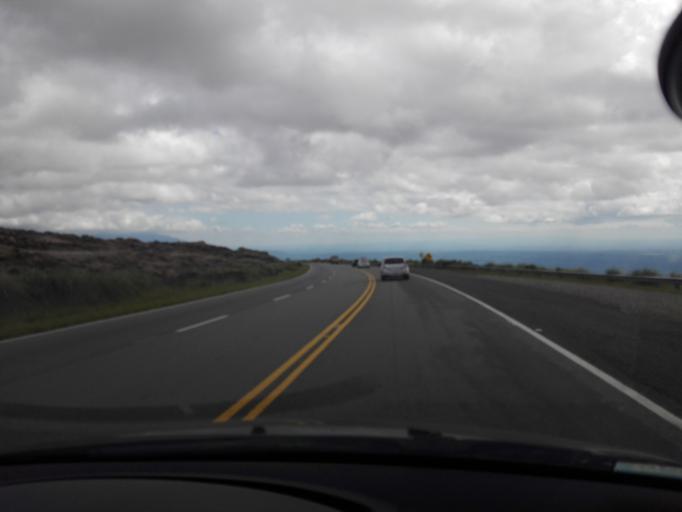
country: AR
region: Cordoba
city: Villa Cura Brochero
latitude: -31.6144
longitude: -64.9095
